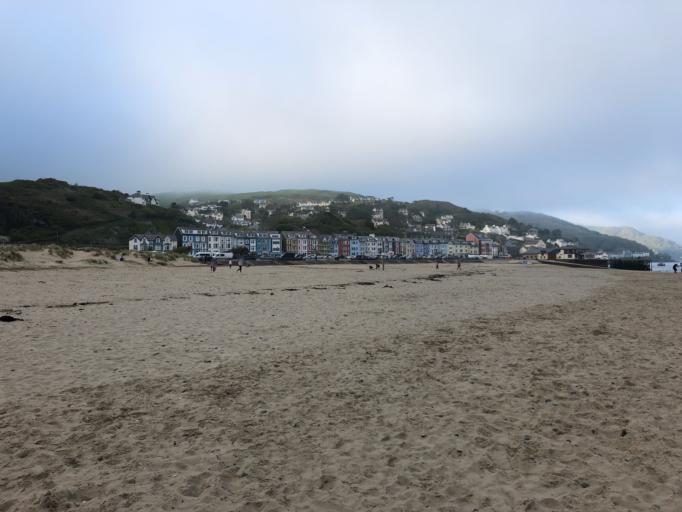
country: GB
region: Wales
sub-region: Gwynedd
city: Tywyn
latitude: 52.5420
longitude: -4.0501
